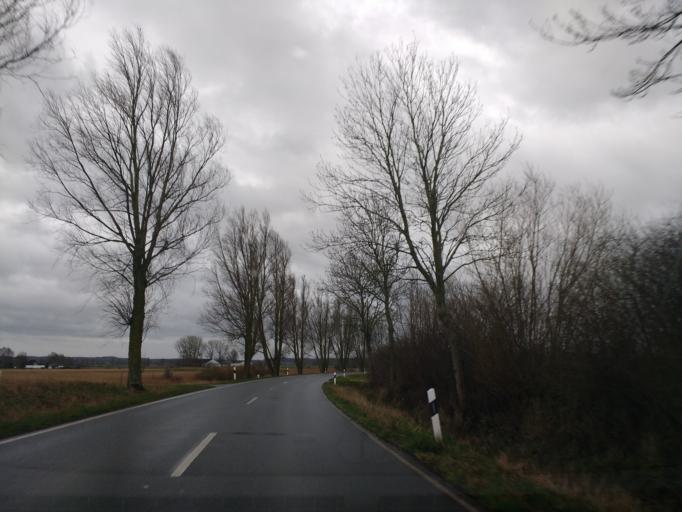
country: DE
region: Schleswig-Holstein
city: Blekendorf
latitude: 54.3125
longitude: 10.6572
